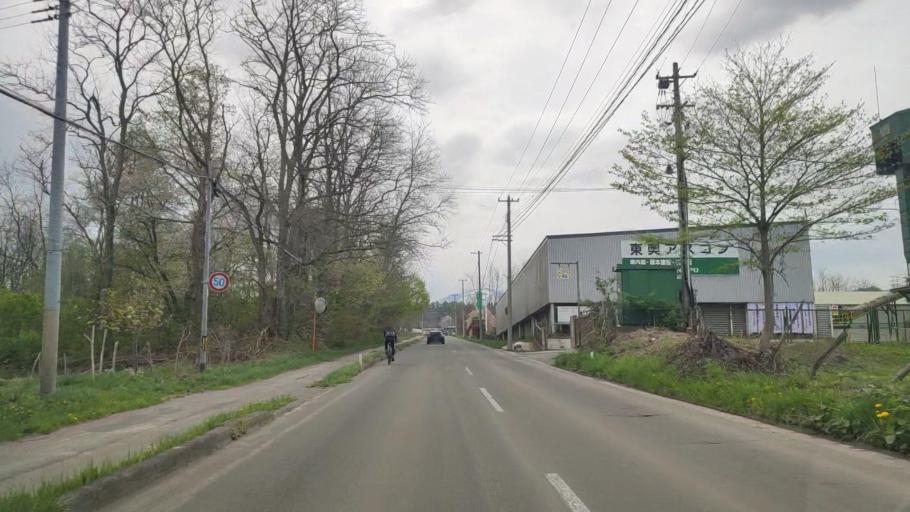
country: JP
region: Aomori
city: Aomori Shi
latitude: 40.7736
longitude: 140.7967
